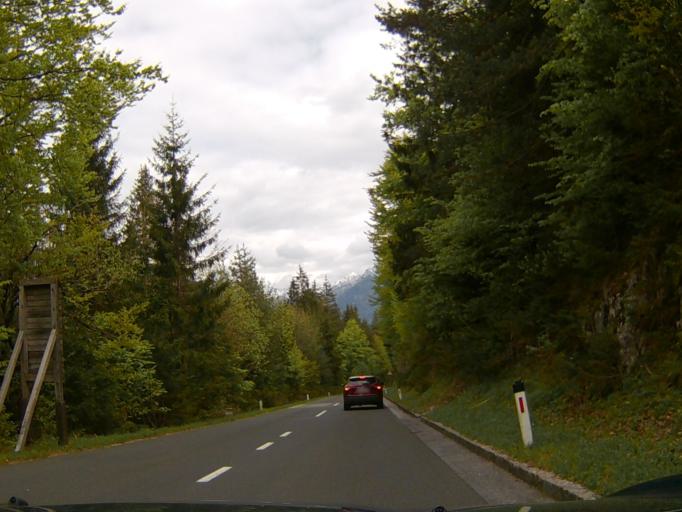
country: AT
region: Carinthia
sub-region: Villach Stadt
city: Villach
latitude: 46.5803
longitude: 13.7839
